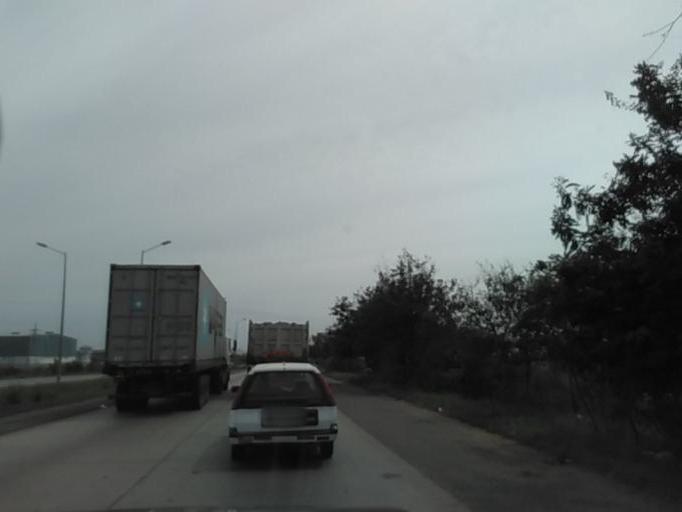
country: GH
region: Greater Accra
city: Tema
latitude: 5.6726
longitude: -0.0475
